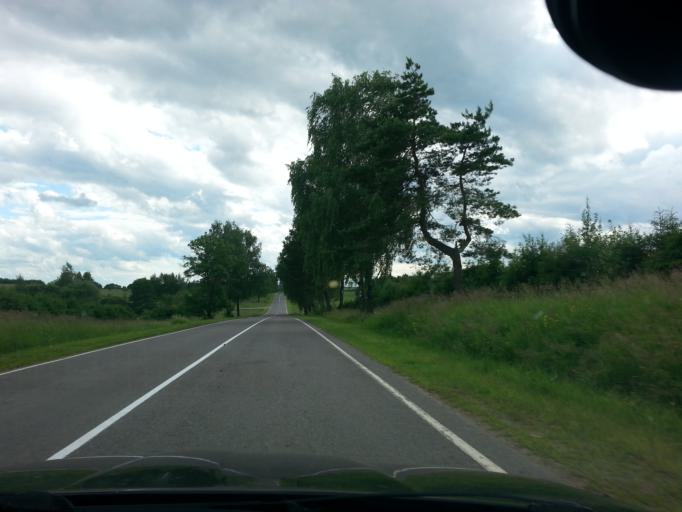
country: BY
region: Minsk
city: Svir
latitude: 54.9082
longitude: 26.3918
